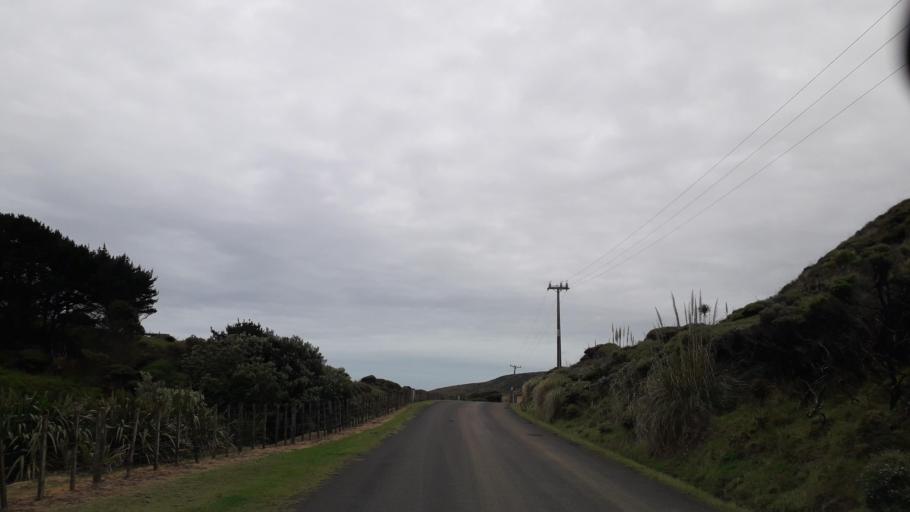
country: NZ
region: Northland
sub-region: Far North District
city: Ahipara
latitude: -35.4366
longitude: 173.2847
